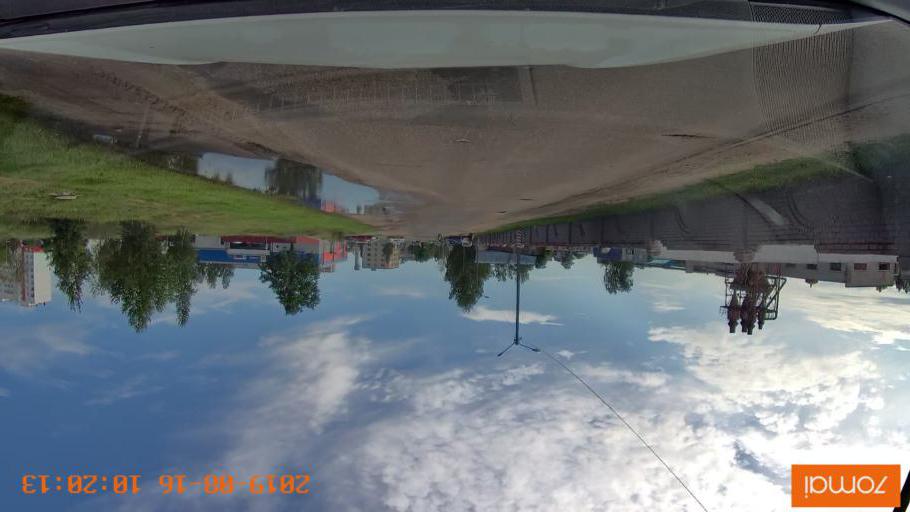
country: BY
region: Mogilev
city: Asipovichy
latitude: 53.3021
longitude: 28.6627
